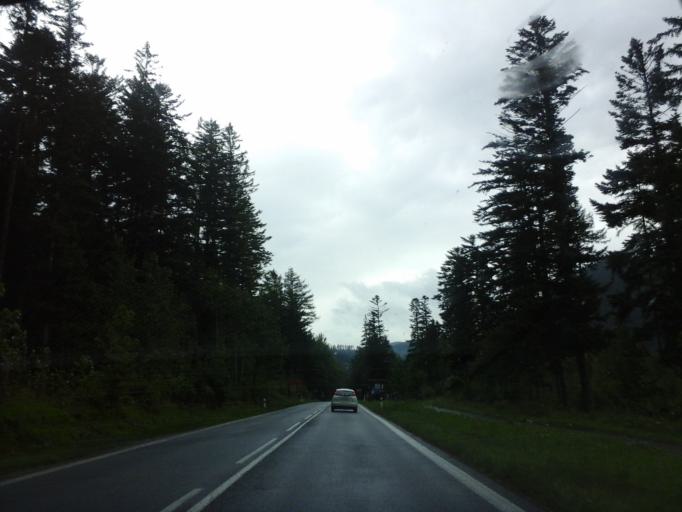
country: SK
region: Presovsky
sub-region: Okres Poprad
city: Zdiar
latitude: 49.2239
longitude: 20.3259
